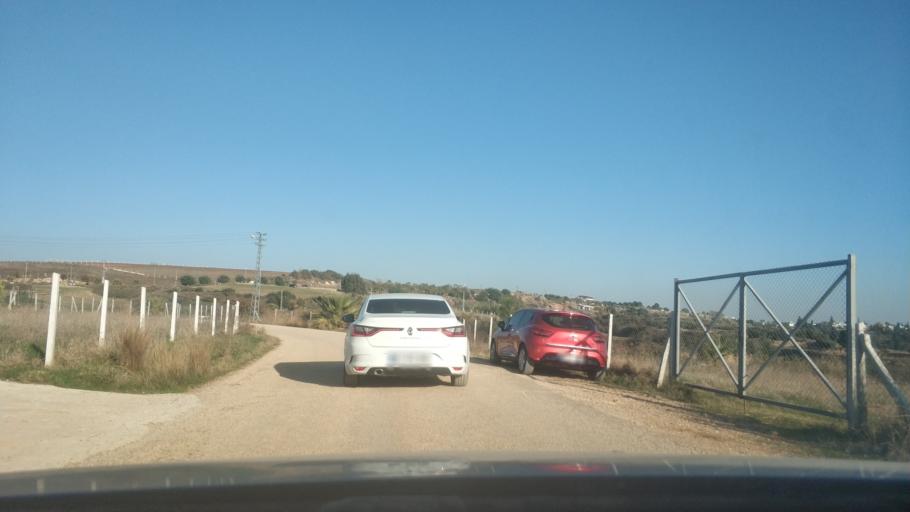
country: TR
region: Adana
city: Adana
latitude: 37.0905
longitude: 35.3027
